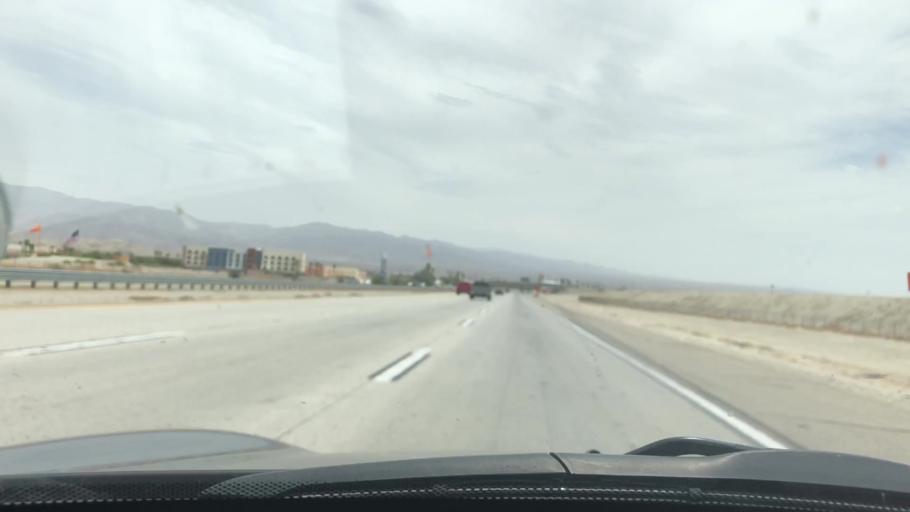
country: US
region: California
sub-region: Riverside County
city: Indio
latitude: 33.7386
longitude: -116.2252
